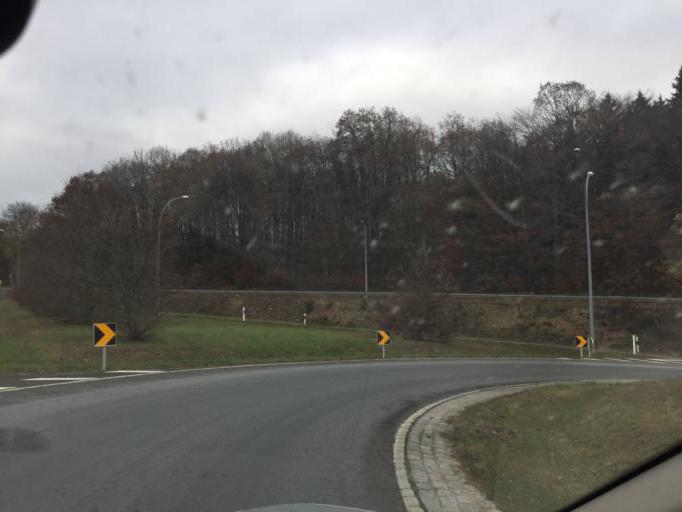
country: LU
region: Diekirch
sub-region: Canton de Wiltz
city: Winseler
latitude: 49.9463
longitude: 5.8780
